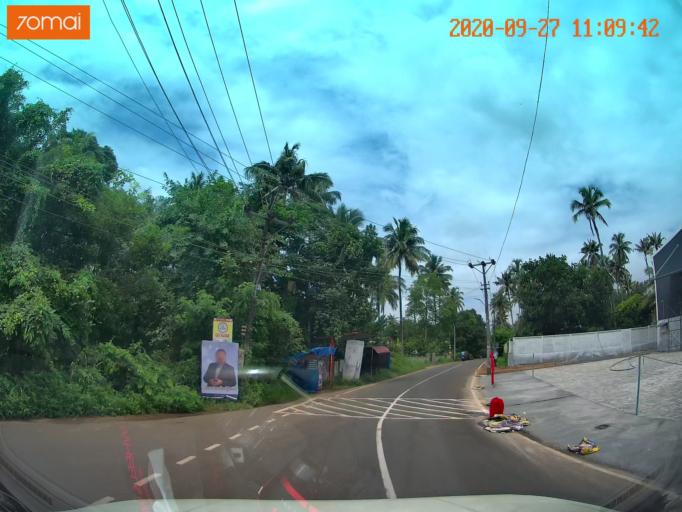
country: IN
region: Kerala
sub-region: Thrissur District
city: Trichur
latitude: 10.4300
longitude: 76.2262
